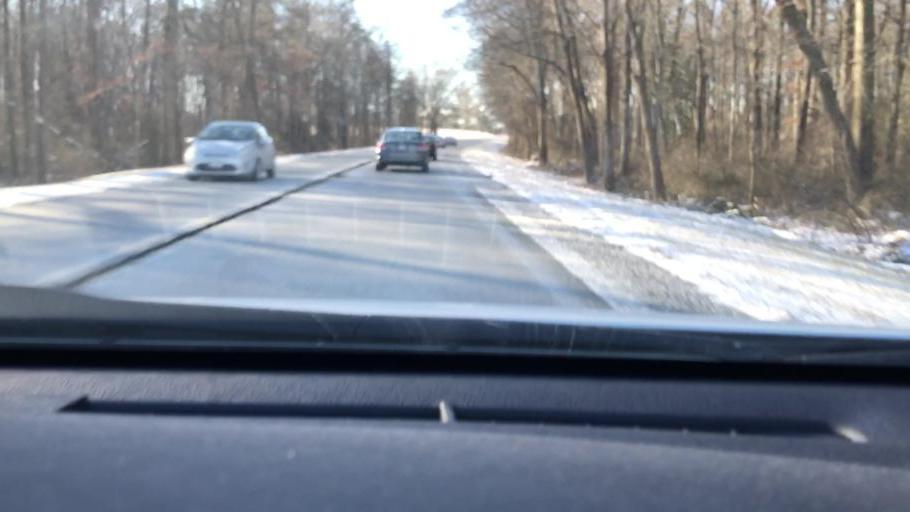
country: US
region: Maryland
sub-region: Prince George's County
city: Goddard
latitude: 39.0198
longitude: -76.8482
